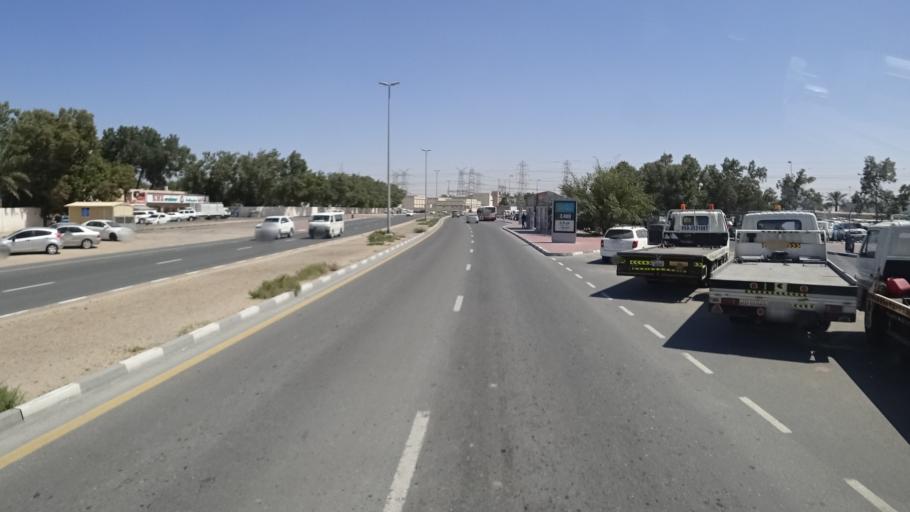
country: AE
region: Ash Shariqah
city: Sharjah
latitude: 25.1745
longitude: 55.3765
